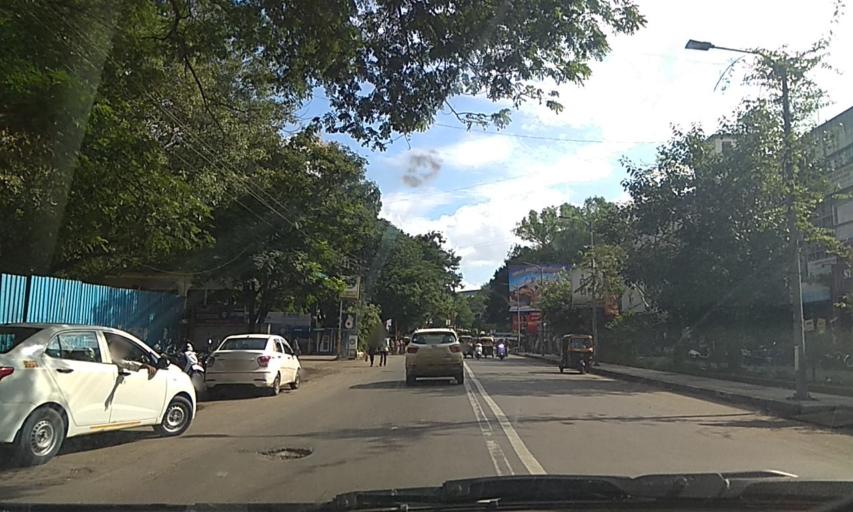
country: IN
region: Maharashtra
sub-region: Pune Division
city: Pune
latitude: 18.5261
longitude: 73.8766
